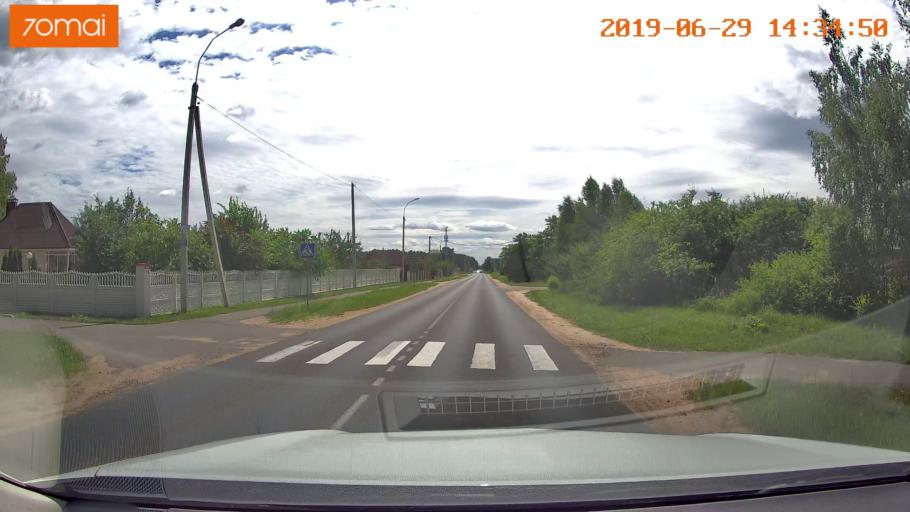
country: BY
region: Minsk
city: Starobin
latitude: 52.7645
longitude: 27.4897
